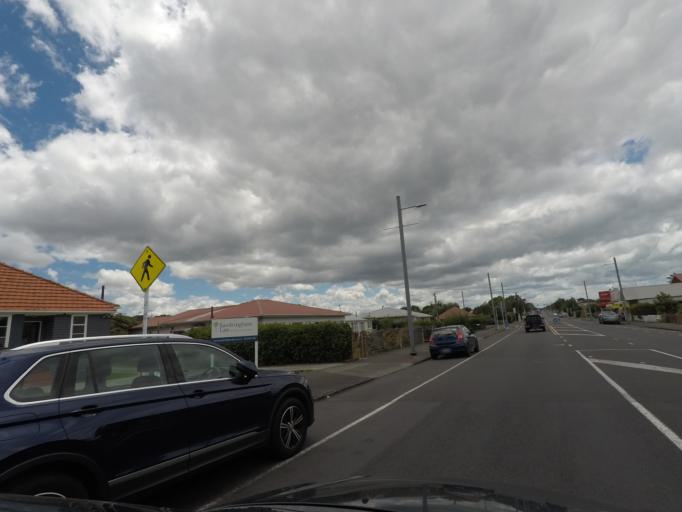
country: NZ
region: Auckland
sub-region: Auckland
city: Auckland
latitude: -36.8912
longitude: 174.7364
